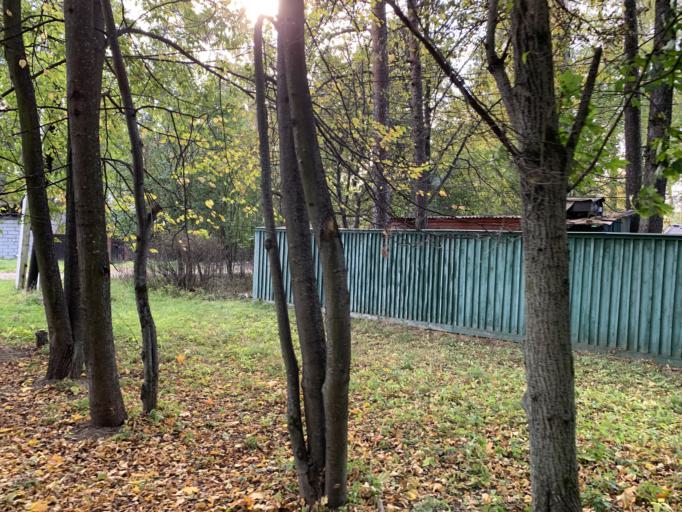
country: RU
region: Moskovskaya
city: Mamontovka
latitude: 55.9832
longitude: 37.8314
